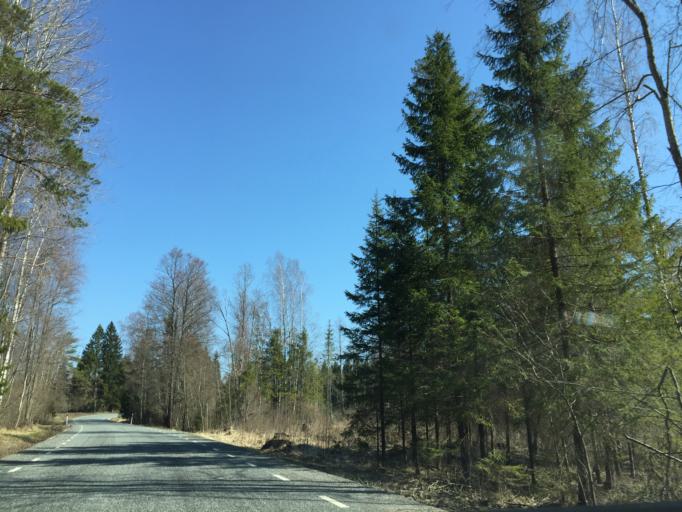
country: EE
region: Tartu
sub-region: Alatskivi vald
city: Kallaste
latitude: 58.5955
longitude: 27.0802
